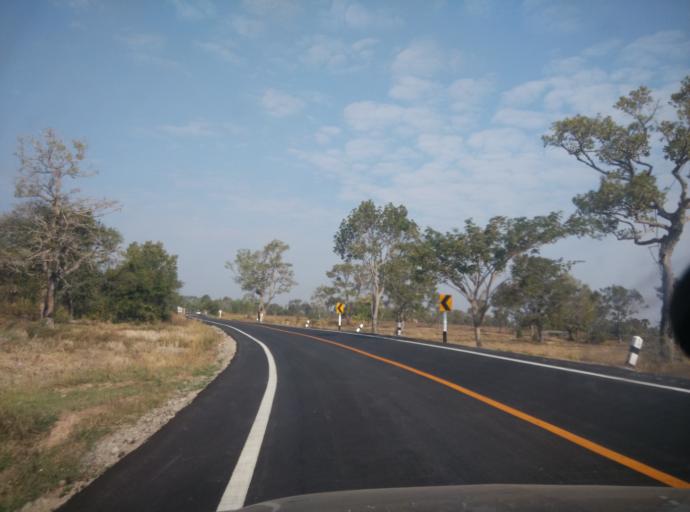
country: TH
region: Sisaket
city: Si Sa Ket
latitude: 15.1209
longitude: 104.2511
